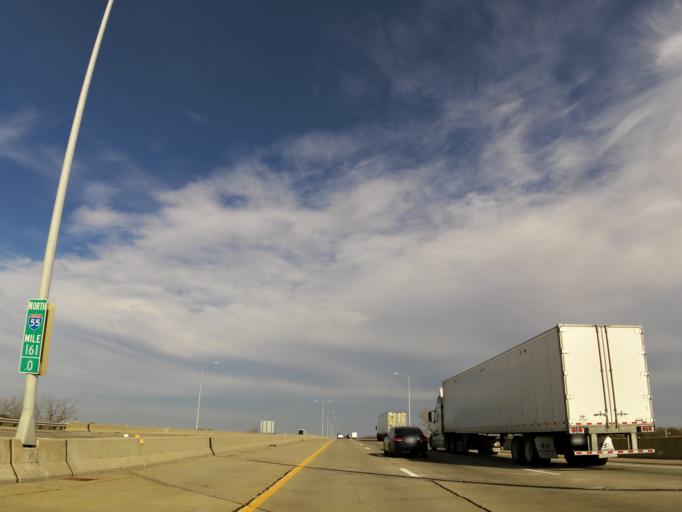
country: US
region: Illinois
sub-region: McLean County
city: Bloomington
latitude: 40.5029
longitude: -89.0286
